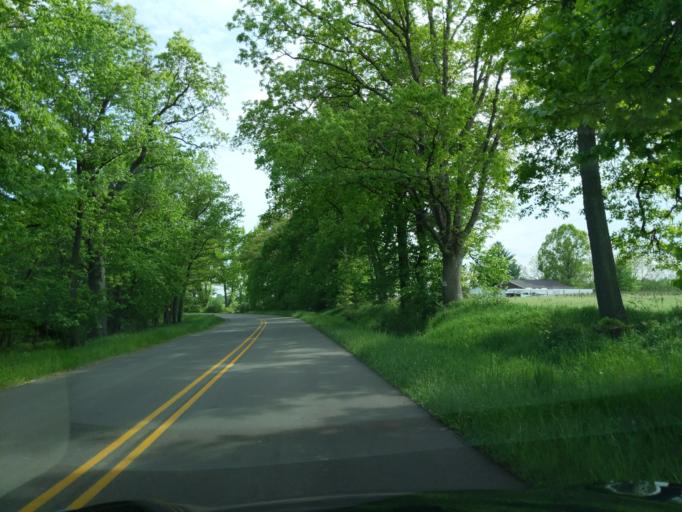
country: US
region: Michigan
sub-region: Ingham County
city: Leslie
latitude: 42.4200
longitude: -84.3567
